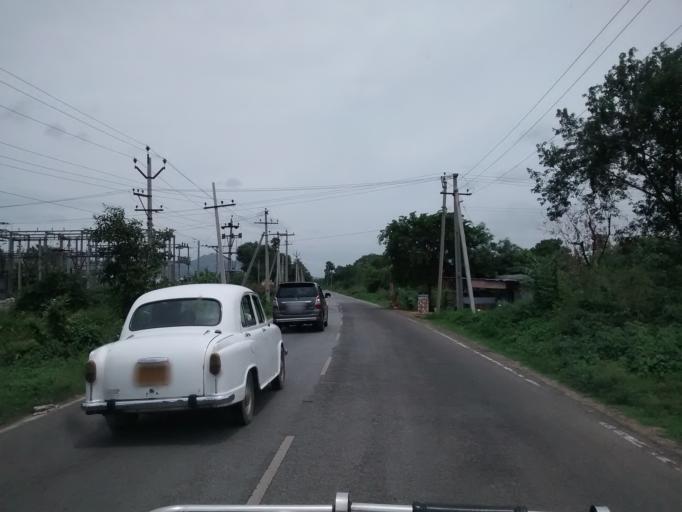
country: IN
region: Andhra Pradesh
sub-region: Chittoor
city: Narasingapuram
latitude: 13.6101
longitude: 79.3476
